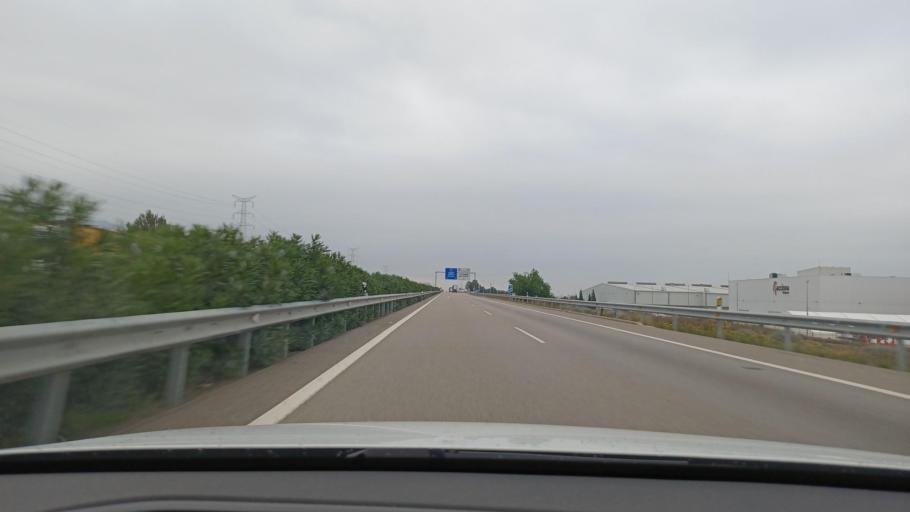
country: ES
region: Valencia
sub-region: Provincia de Castello
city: Chilches
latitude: 39.8130
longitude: -0.2140
